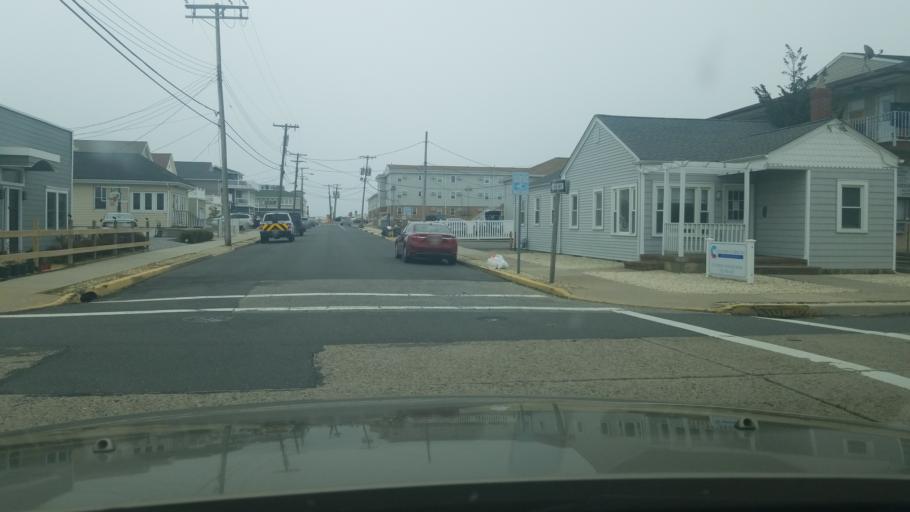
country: US
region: New Jersey
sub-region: Ocean County
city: Seaside Heights
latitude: 39.9358
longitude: -74.0747
